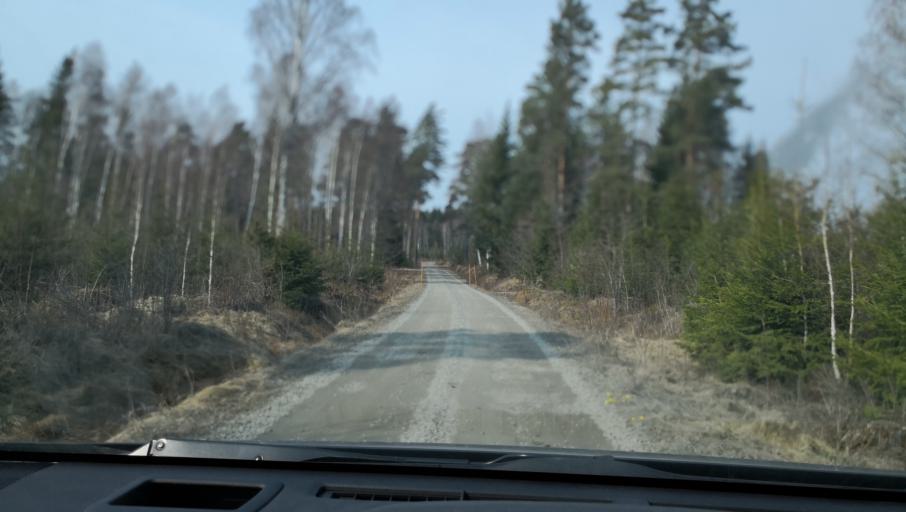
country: SE
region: OErebro
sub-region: Lindesbergs Kommun
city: Frovi
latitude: 59.3727
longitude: 15.4260
